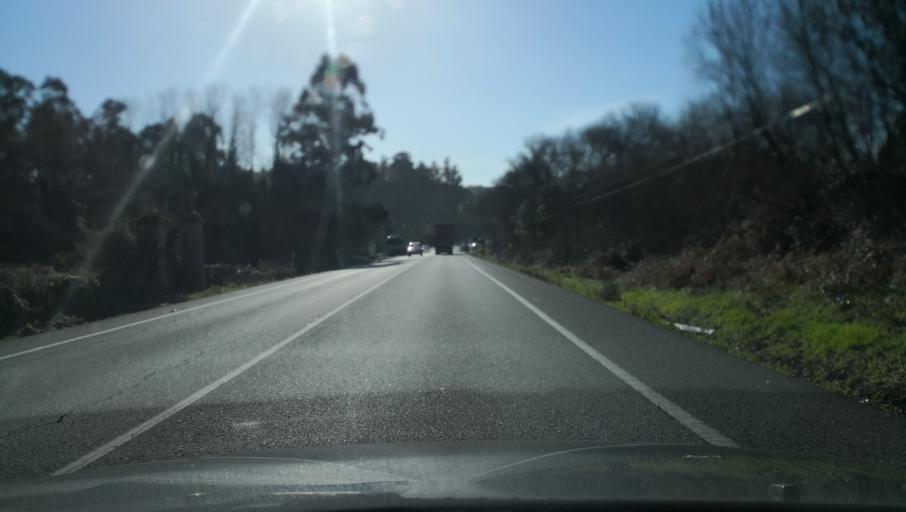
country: ES
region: Galicia
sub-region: Provincia da Coruna
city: Vedra
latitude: 42.8079
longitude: -8.4784
